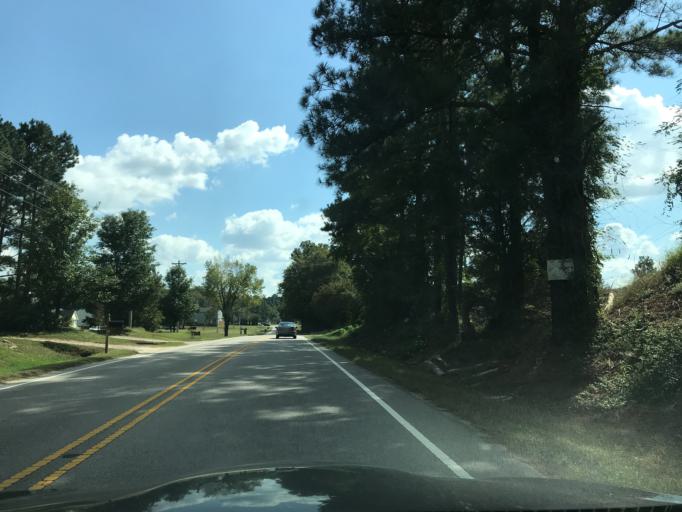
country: US
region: North Carolina
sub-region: Wake County
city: Rolesville
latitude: 35.8999
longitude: -78.5244
